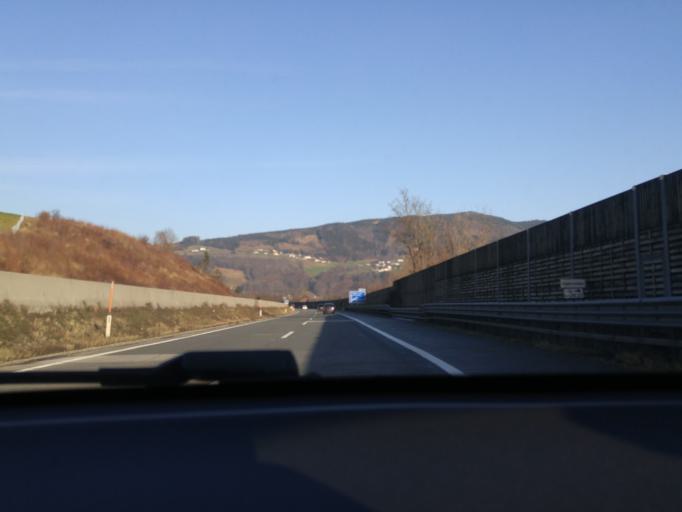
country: AT
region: Upper Austria
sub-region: Politischer Bezirk Vocklabruck
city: Mondsee
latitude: 47.8505
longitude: 13.3249
